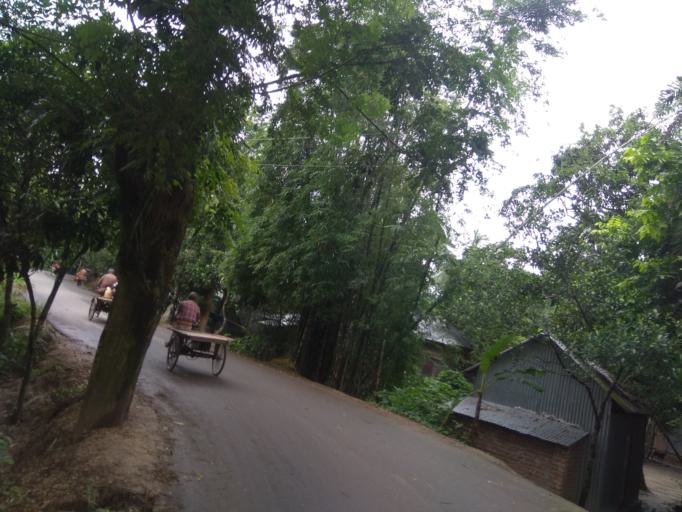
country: BD
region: Dhaka
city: Dohar
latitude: 23.4305
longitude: 90.0705
